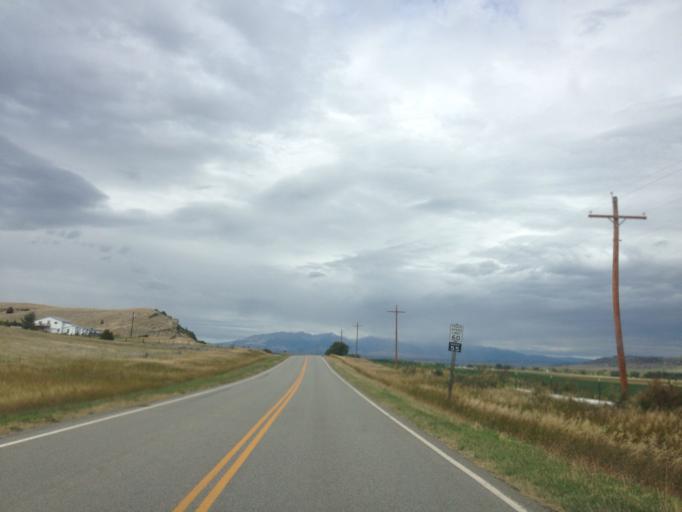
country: US
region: Montana
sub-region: Sweet Grass County
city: Big Timber
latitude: 45.7768
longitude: -109.8084
